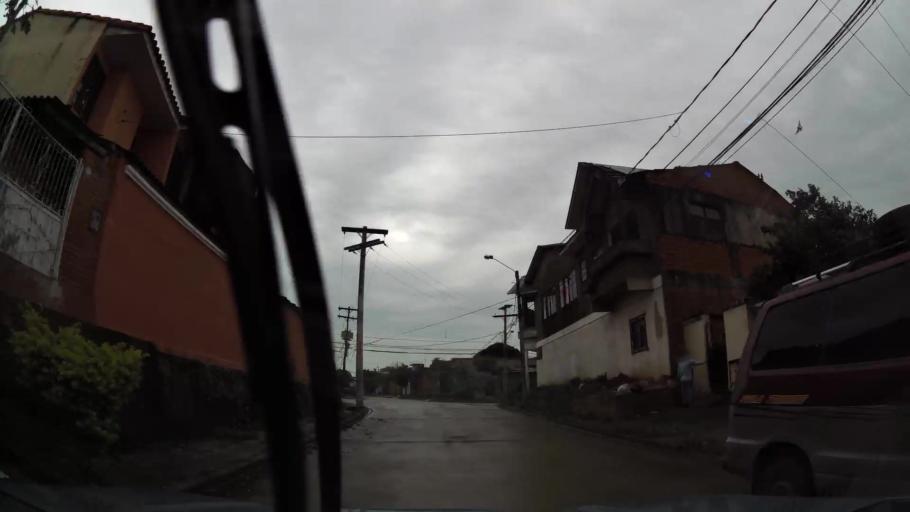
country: BO
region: Santa Cruz
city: Santa Cruz de la Sierra
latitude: -17.8064
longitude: -63.1913
